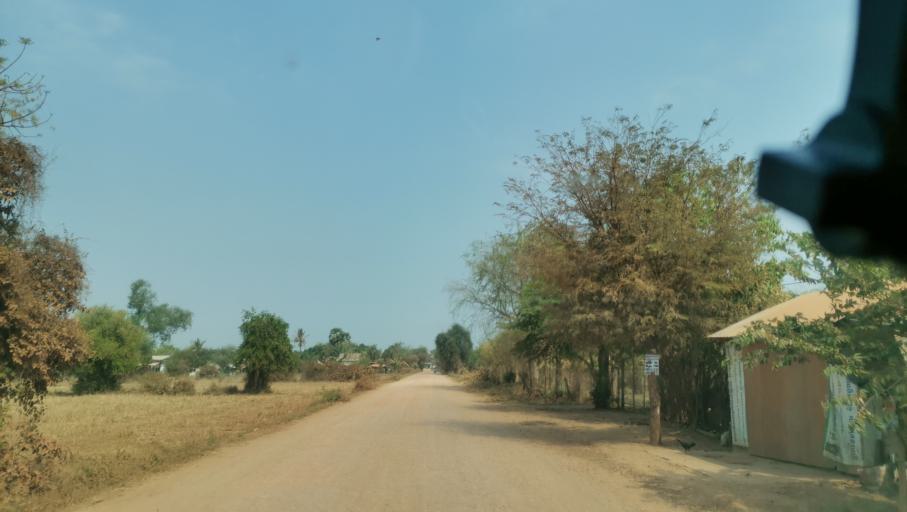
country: KH
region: Battambang
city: Battambang
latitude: 13.0689
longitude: 103.1695
